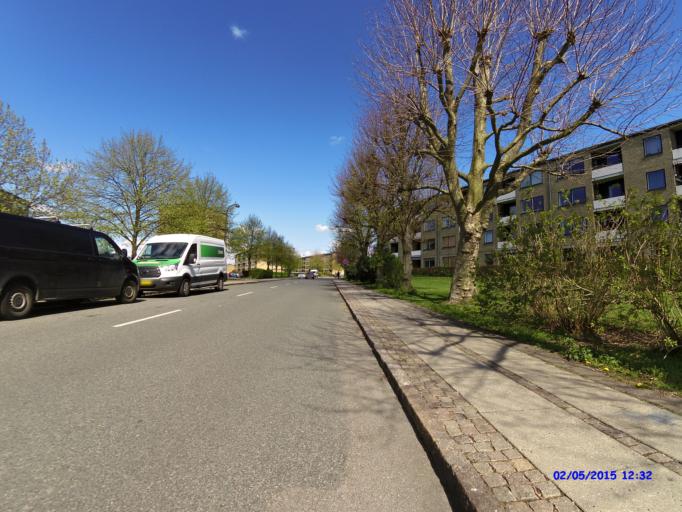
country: DK
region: Capital Region
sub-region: Gladsaxe Municipality
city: Buddinge
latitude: 55.7358
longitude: 12.5197
